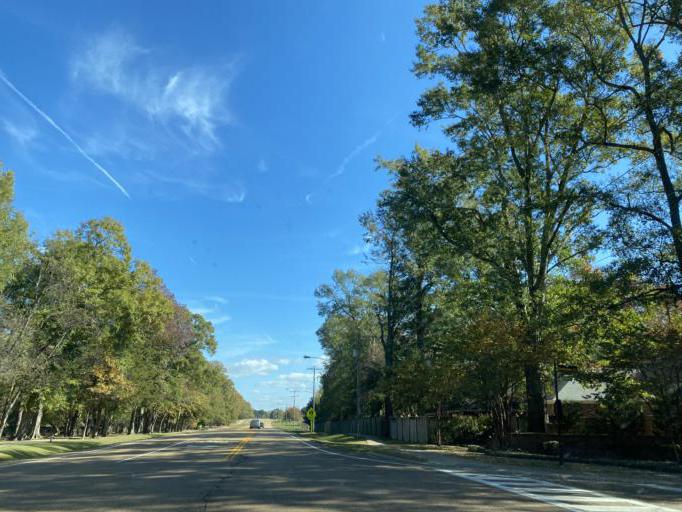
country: US
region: Mississippi
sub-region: Madison County
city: Madison
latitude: 32.4575
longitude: -90.0992
